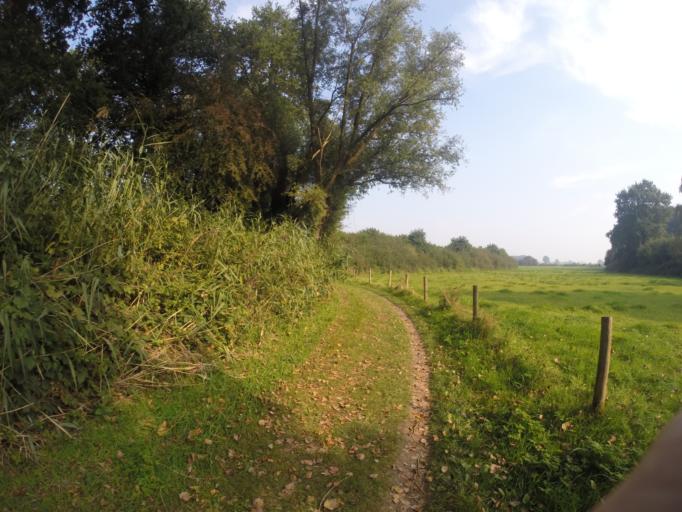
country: NL
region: Gelderland
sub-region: Gemeente Lochem
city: Laren
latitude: 52.1590
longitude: 6.3495
